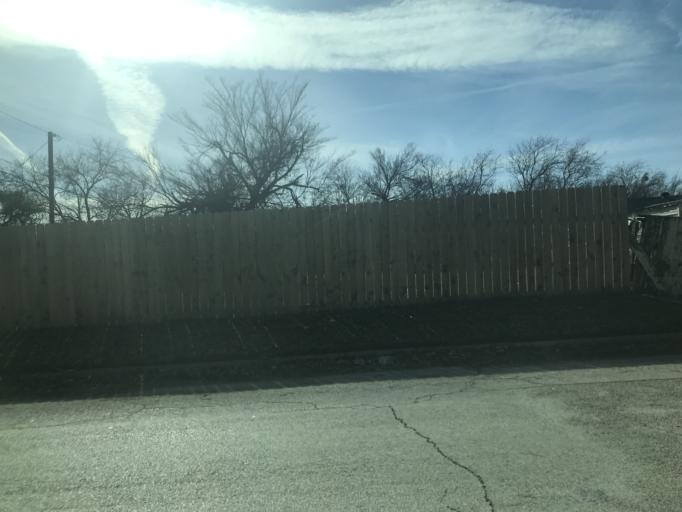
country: US
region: Texas
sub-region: Taylor County
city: Abilene
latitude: 32.4868
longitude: -99.7367
